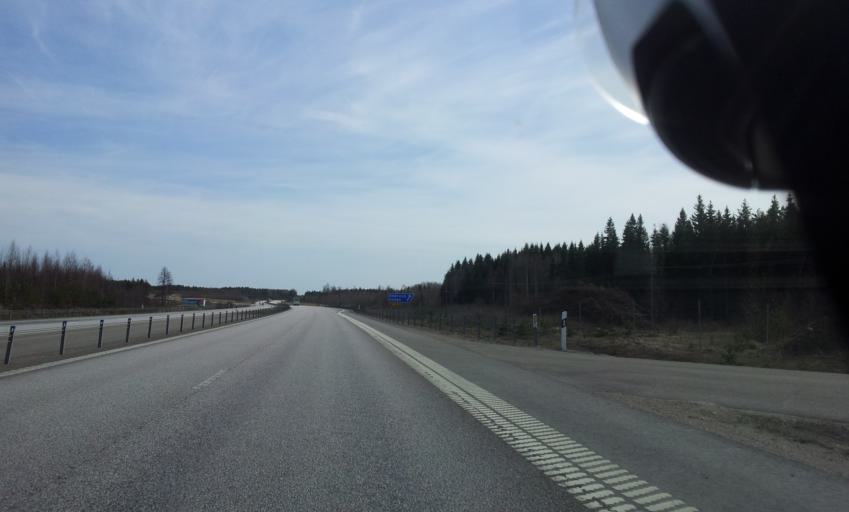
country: SE
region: Uppsala
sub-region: Osthammars Kommun
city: Bjorklinge
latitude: 60.1746
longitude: 17.5126
